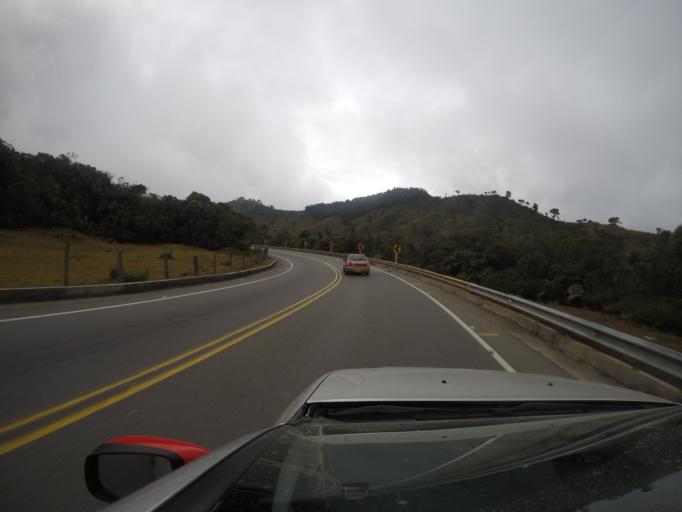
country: CO
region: Tolima
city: Herveo
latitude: 5.0710
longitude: -75.2867
